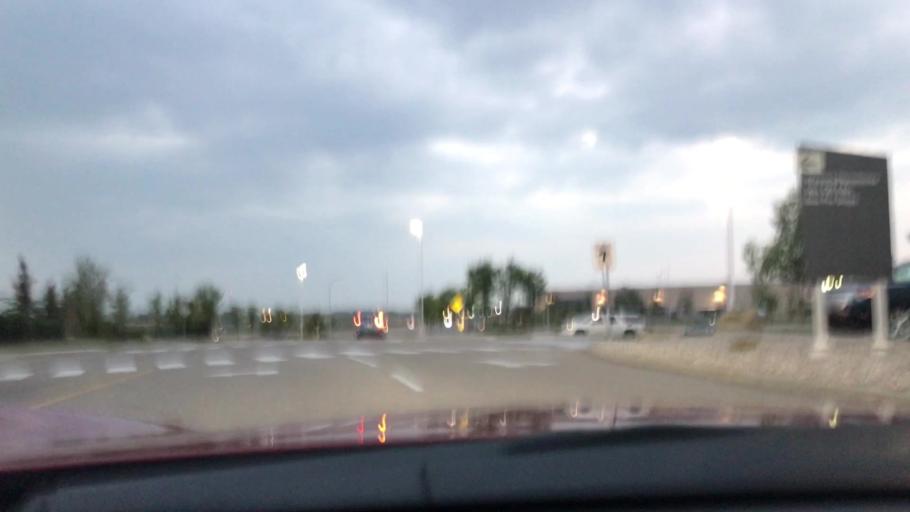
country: CA
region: Alberta
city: Airdrie
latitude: 51.2059
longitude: -113.9920
